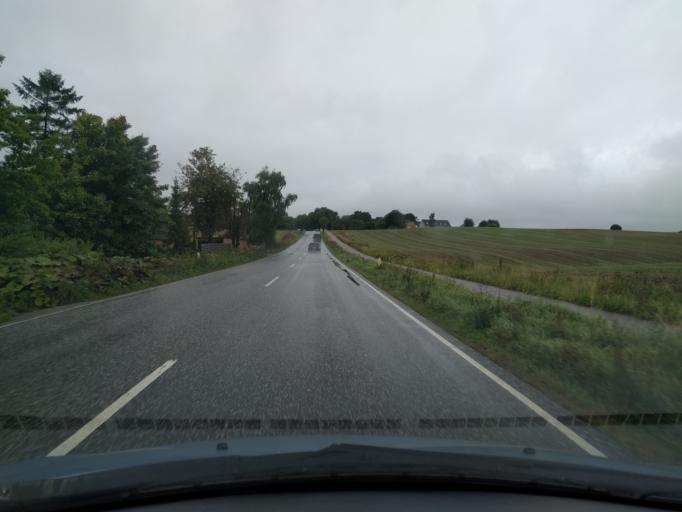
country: DK
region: Zealand
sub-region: Naestved Kommune
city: Fuglebjerg
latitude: 55.2714
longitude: 11.6361
